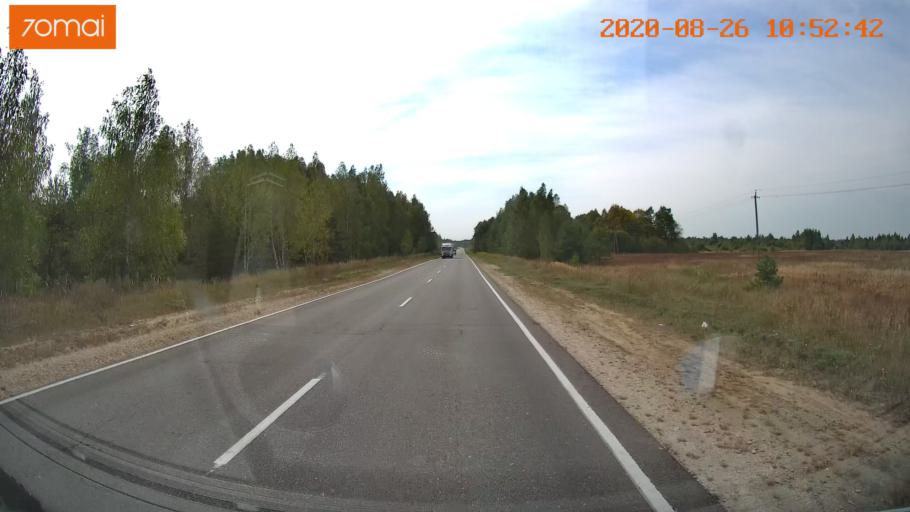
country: RU
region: Rjazan
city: Lashma
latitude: 54.6528
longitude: 41.1534
